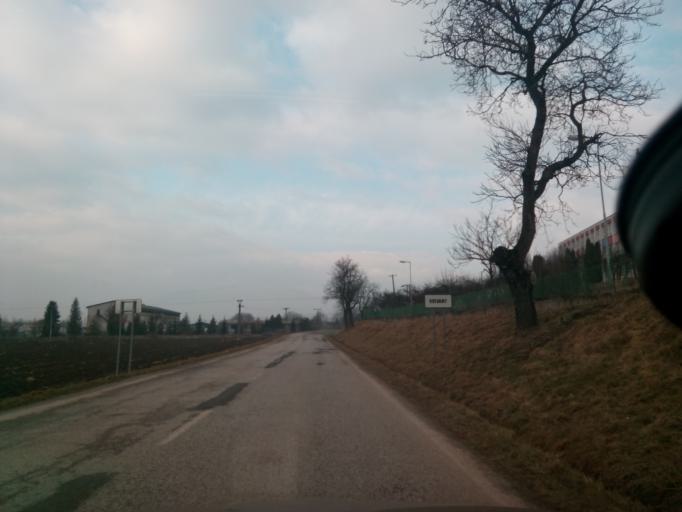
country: SK
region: Presovsky
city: Lipany
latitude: 49.1689
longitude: 20.9213
